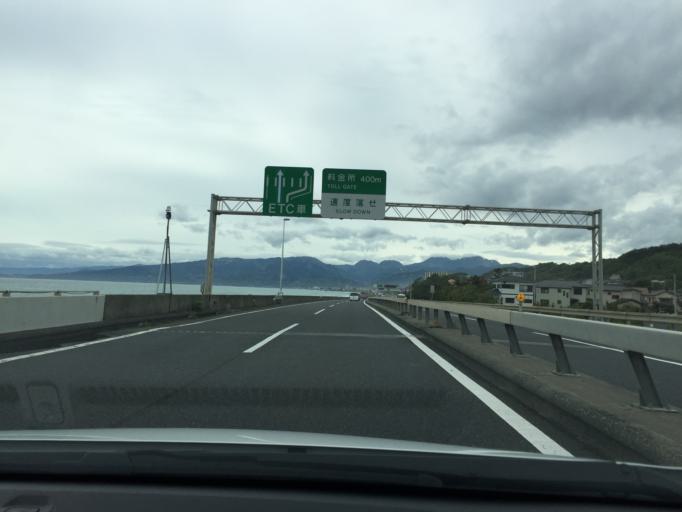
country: JP
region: Kanagawa
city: Ninomiya
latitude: 35.2890
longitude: 139.2391
